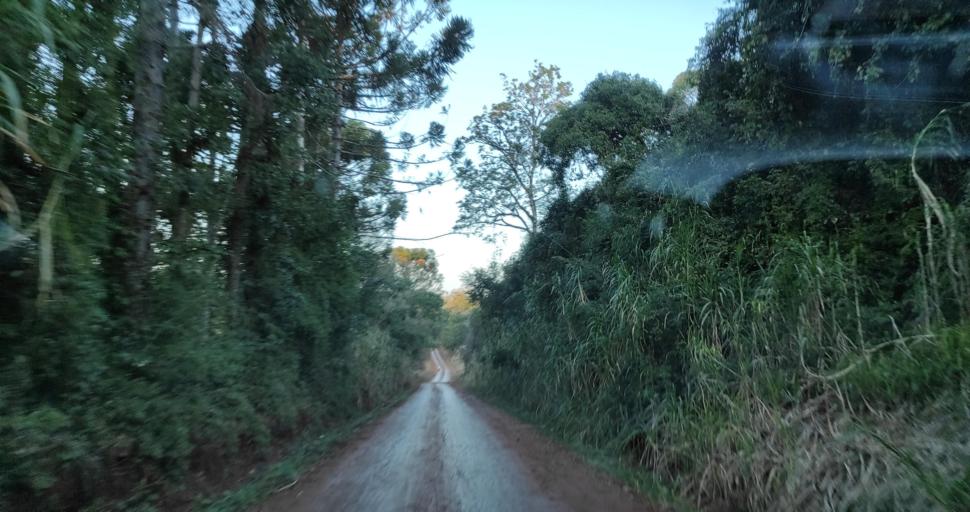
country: AR
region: Misiones
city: Capiovi
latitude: -26.8788
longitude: -55.0911
